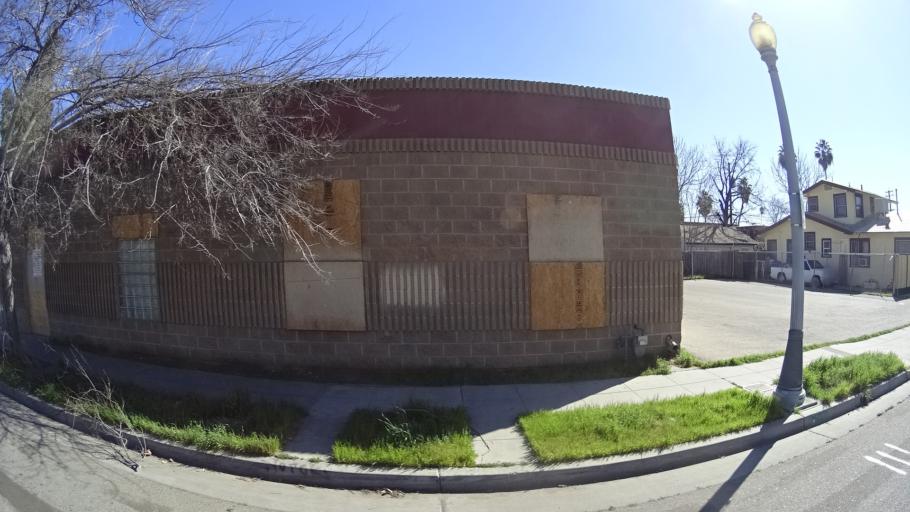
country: US
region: California
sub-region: Fresno County
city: Fresno
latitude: 36.7456
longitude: -119.7815
